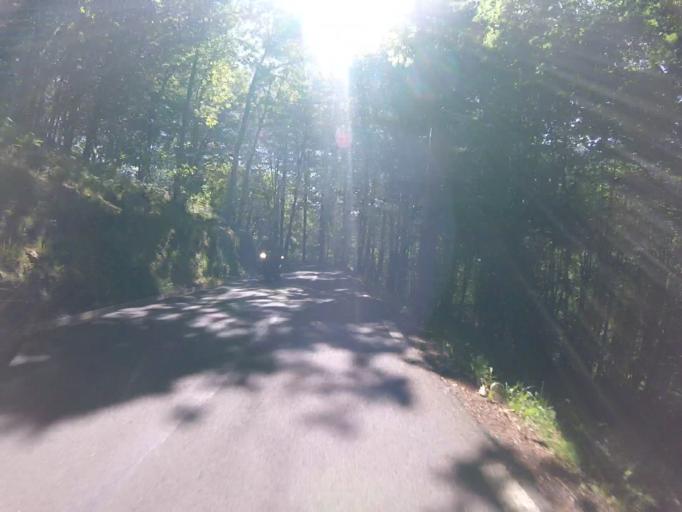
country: ES
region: Basque Country
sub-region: Provincia de Guipuzcoa
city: Beizama
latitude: 43.1239
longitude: -2.1699
